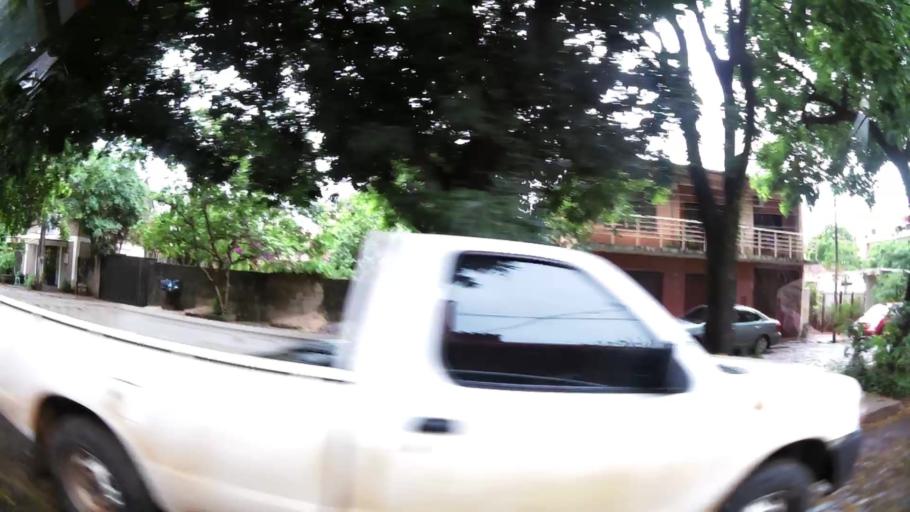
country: PY
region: Alto Parana
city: Ciudad del Este
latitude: -25.5078
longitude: -54.6446
